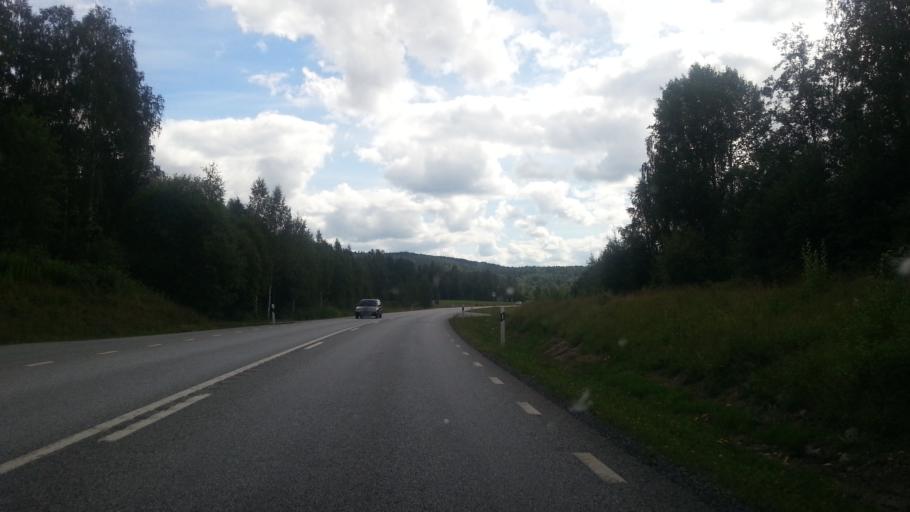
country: SE
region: OErebro
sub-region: Ljusnarsbergs Kommun
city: Kopparberg
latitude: 59.8387
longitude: 15.0914
